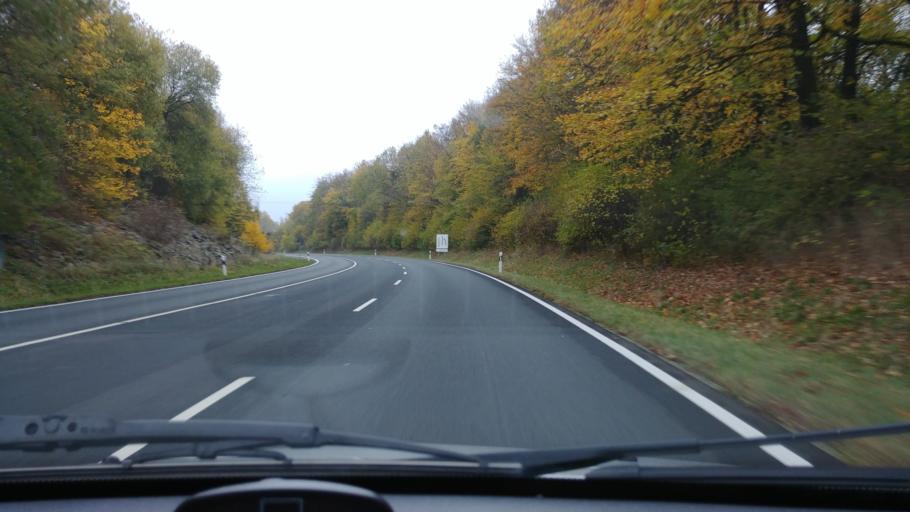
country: DE
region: Rheinland-Pfalz
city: Langenhahn
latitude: 50.5909
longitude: 7.9133
